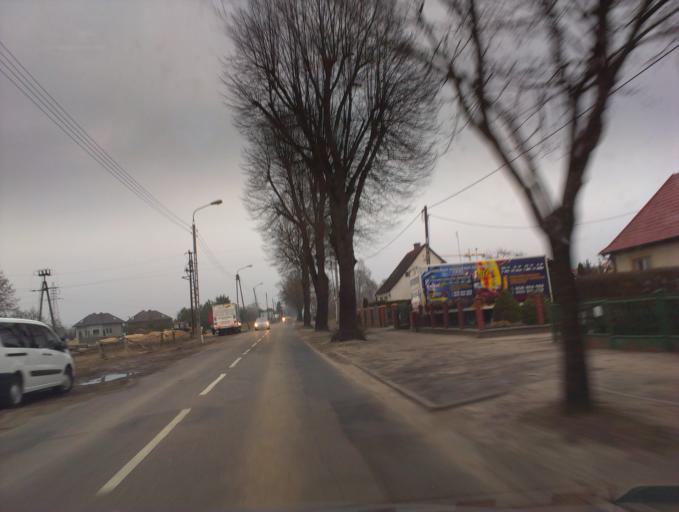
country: PL
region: Greater Poland Voivodeship
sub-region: Powiat pilski
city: Pila
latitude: 53.1762
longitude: 16.7485
